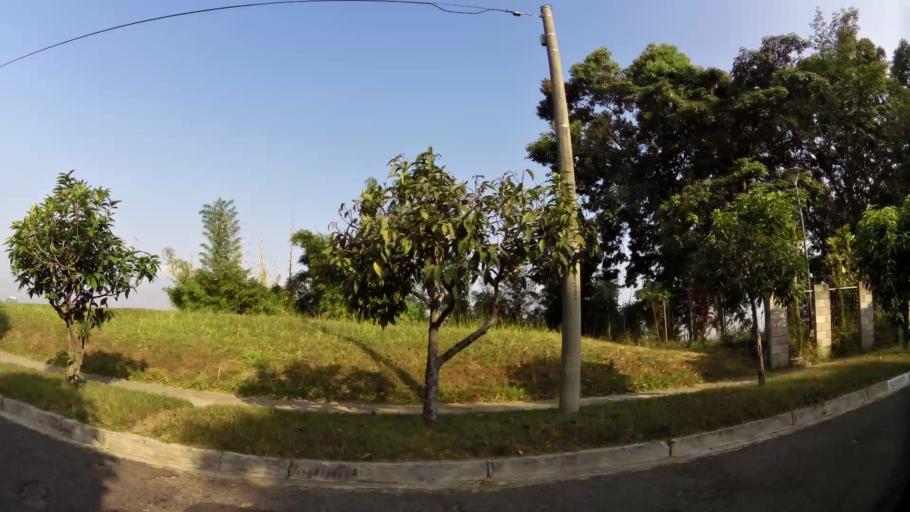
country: SV
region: San Salvador
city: San Salvador
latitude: 13.6801
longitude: -89.2210
